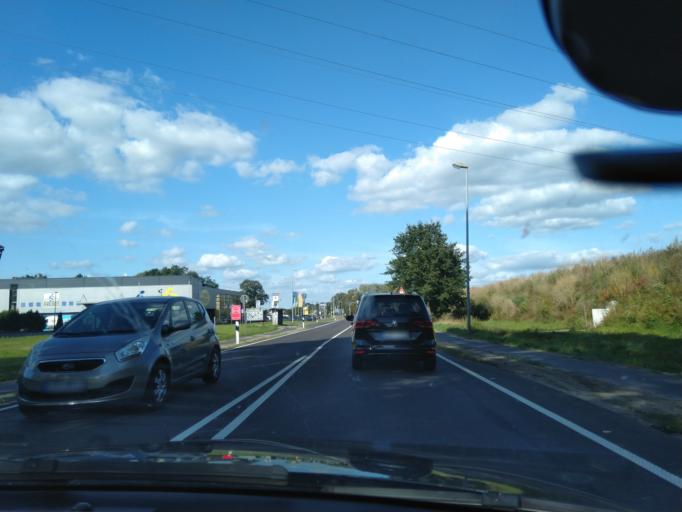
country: DE
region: Lower Saxony
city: Leer
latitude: 53.2572
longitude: 7.4588
